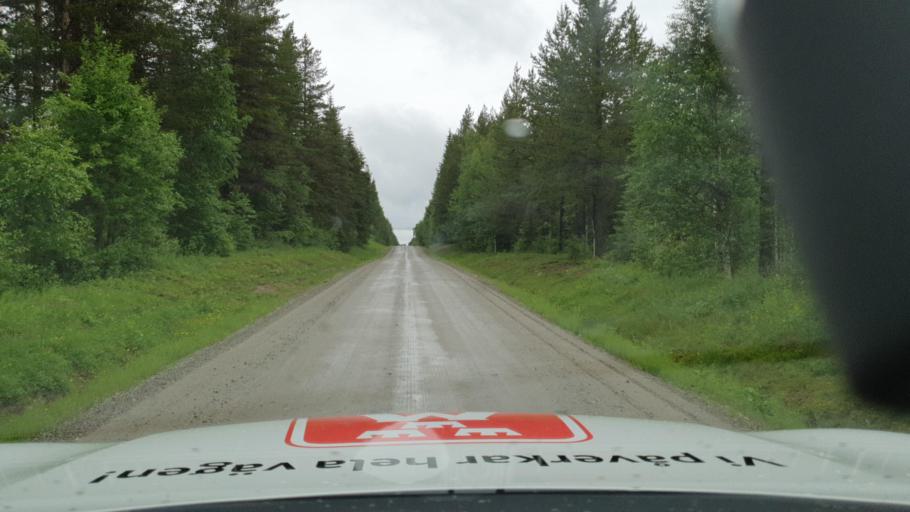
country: SE
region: Vaesterbotten
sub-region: Dorotea Kommun
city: Dorotea
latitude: 64.0613
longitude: 16.7151
